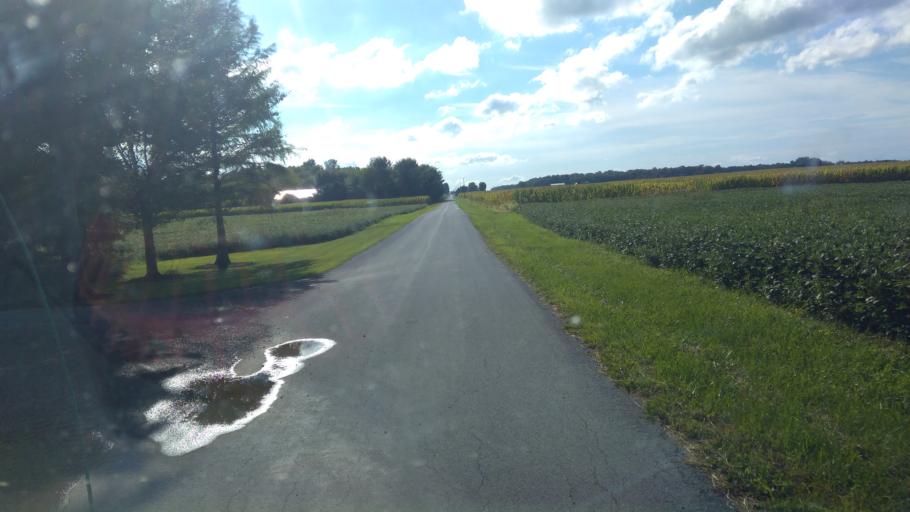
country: US
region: Ohio
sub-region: Hardin County
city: Kenton
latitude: 40.7176
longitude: -83.6602
